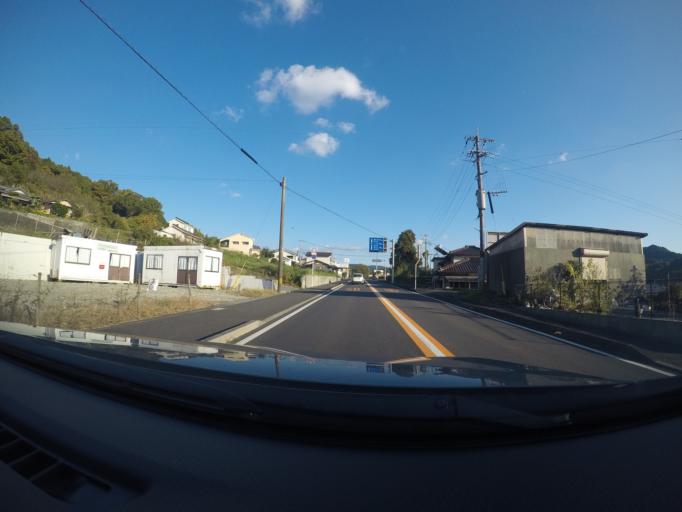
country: JP
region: Kumamoto
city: Minamata
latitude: 32.2111
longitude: 130.4108
